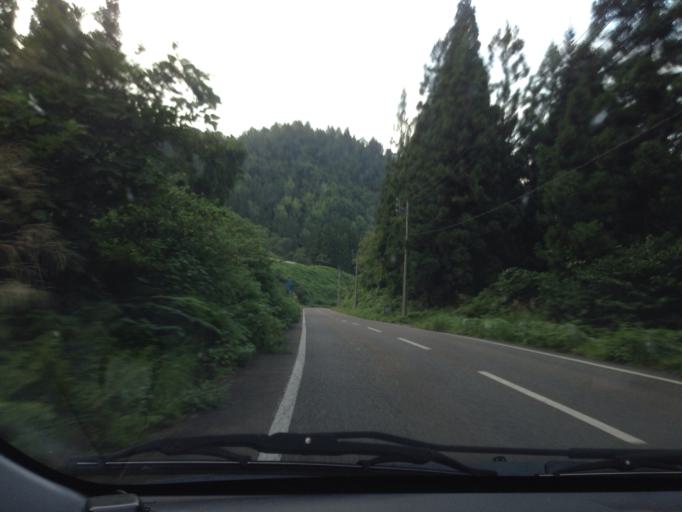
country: JP
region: Fukushima
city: Kitakata
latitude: 37.4767
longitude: 139.6905
